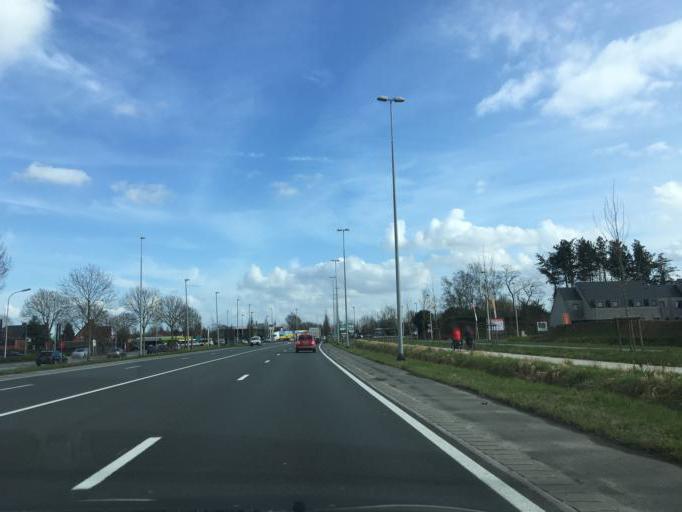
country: BE
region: Flanders
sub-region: Provincie West-Vlaanderen
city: Izegem
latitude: 50.9157
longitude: 3.1940
